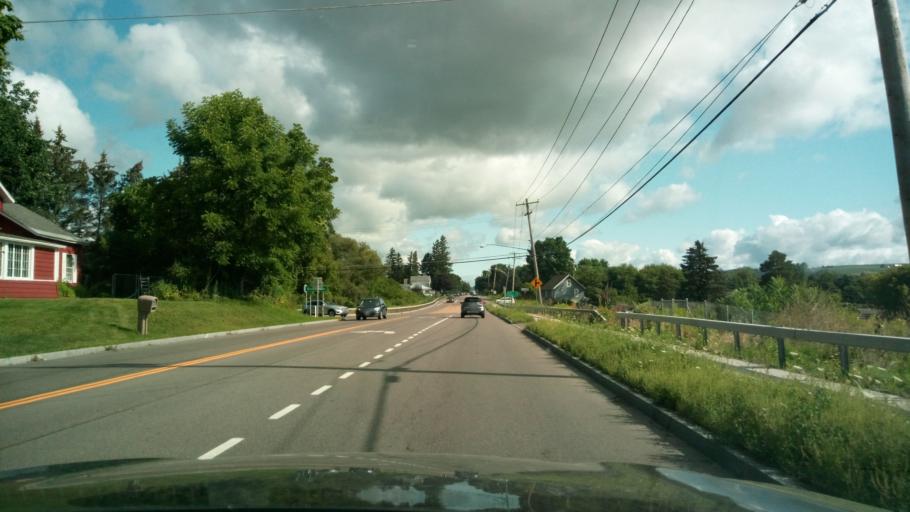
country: US
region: New York
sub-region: Cortland County
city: Cortland
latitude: 42.6143
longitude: -76.1955
